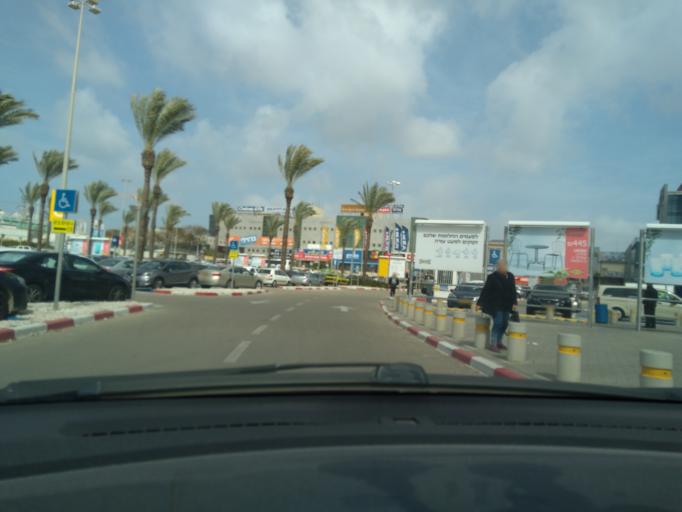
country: IL
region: Central District
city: Even Yehuda
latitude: 32.2736
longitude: 34.8603
